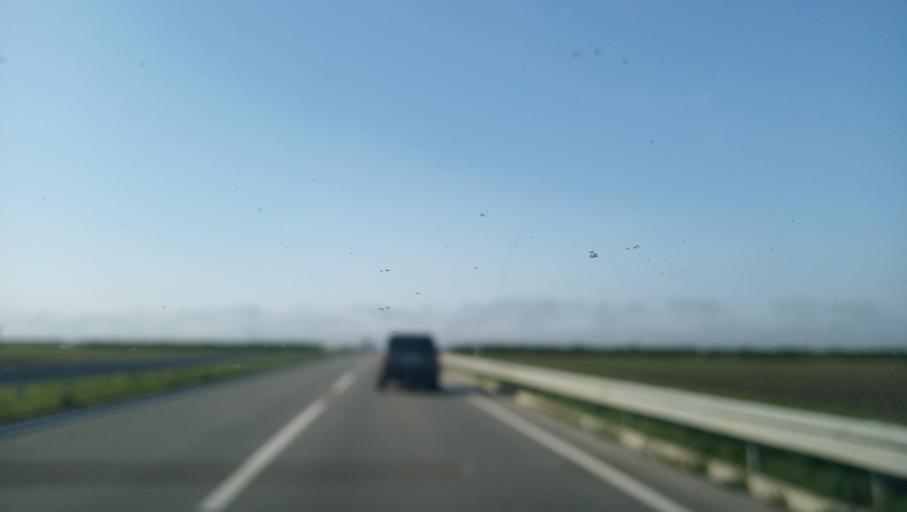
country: RS
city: Pavlis
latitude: 45.1055
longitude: 21.2612
